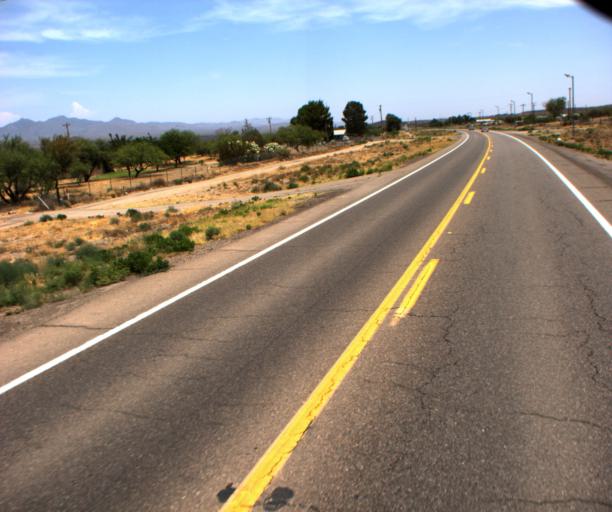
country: US
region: Arizona
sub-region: Graham County
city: Bylas
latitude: 33.1169
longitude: -110.1069
